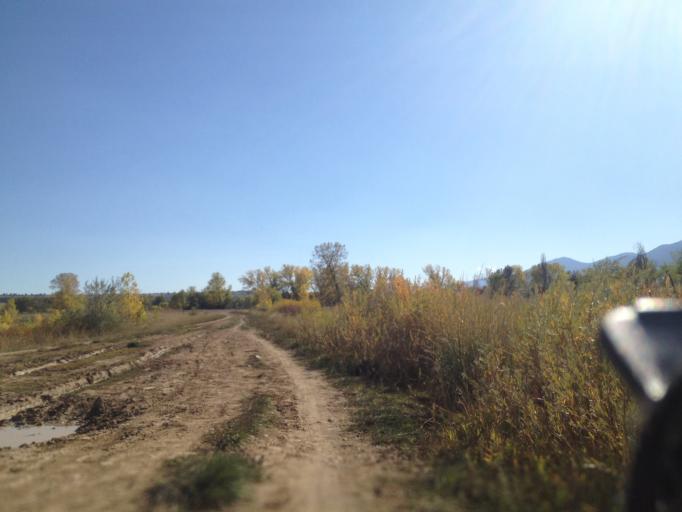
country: US
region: Colorado
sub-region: Boulder County
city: Boulder
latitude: 39.9735
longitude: -105.2339
